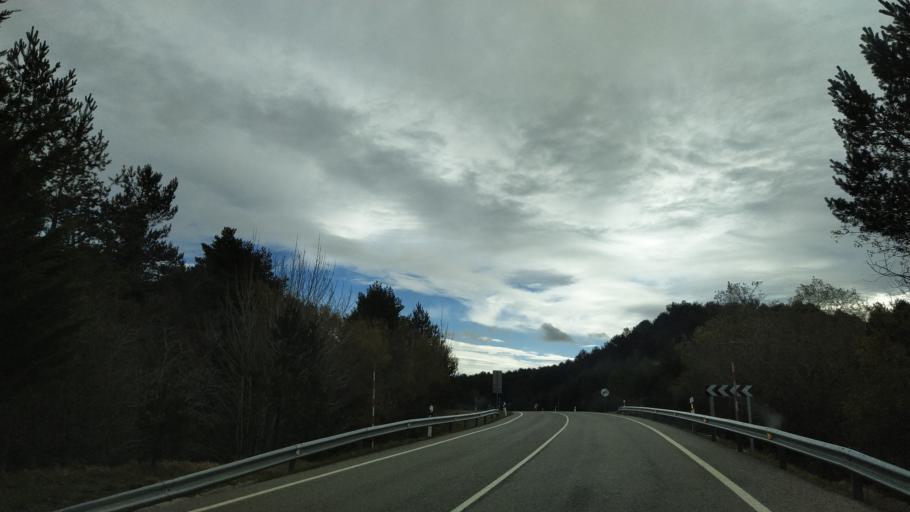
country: ES
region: Castille and Leon
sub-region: Provincia de Burgos
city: Arija
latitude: 42.9947
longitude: -3.8347
